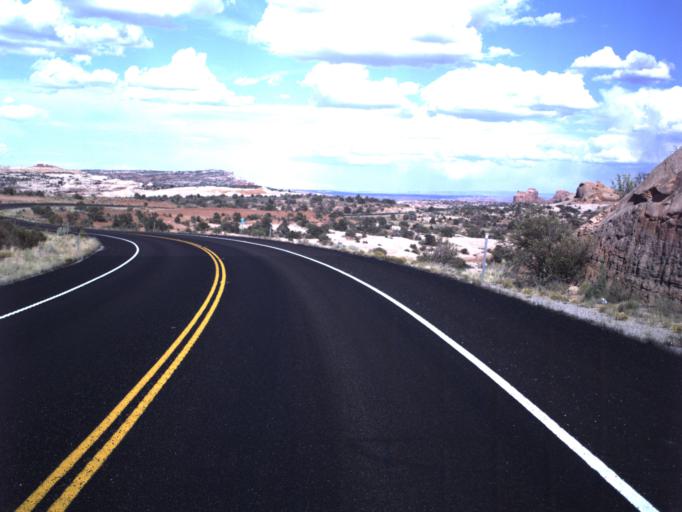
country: US
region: Utah
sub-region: Grand County
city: Moab
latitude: 38.6374
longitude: -109.7527
